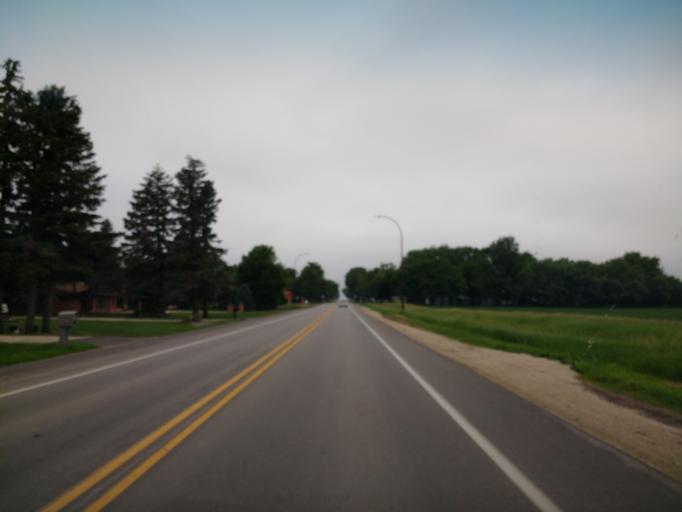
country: US
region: Iowa
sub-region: O'Brien County
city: Sanborn
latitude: 43.1861
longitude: -95.6488
